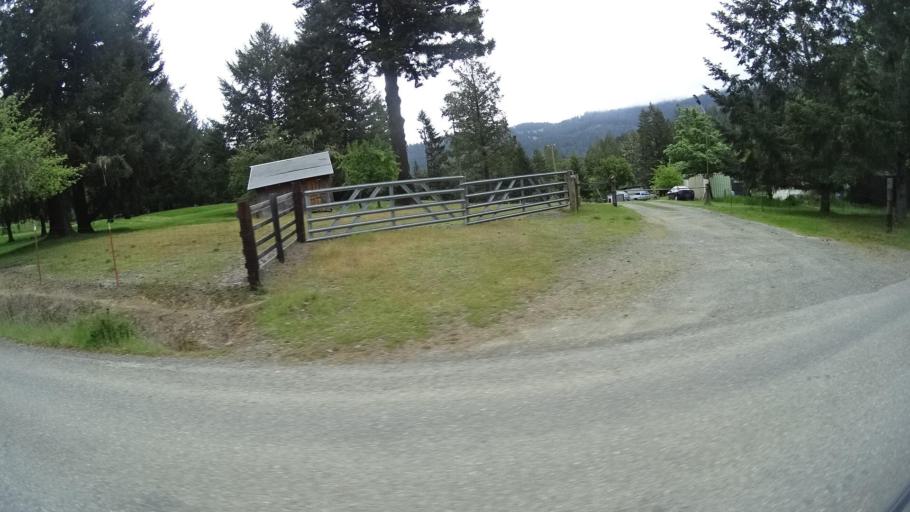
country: US
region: California
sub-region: Humboldt County
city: Redway
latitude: 40.2842
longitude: -123.7988
